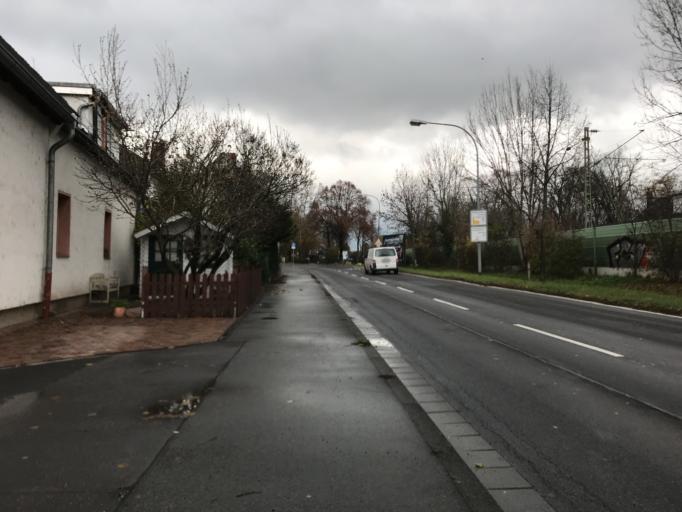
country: DE
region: Rheinland-Pfalz
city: Bodenheim
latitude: 49.9583
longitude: 8.3129
